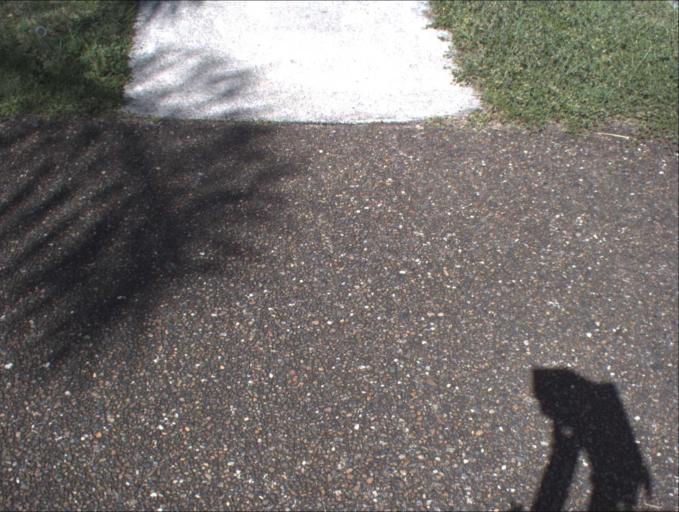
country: AU
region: Queensland
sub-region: Logan
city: Waterford West
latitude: -27.7041
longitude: 153.1669
